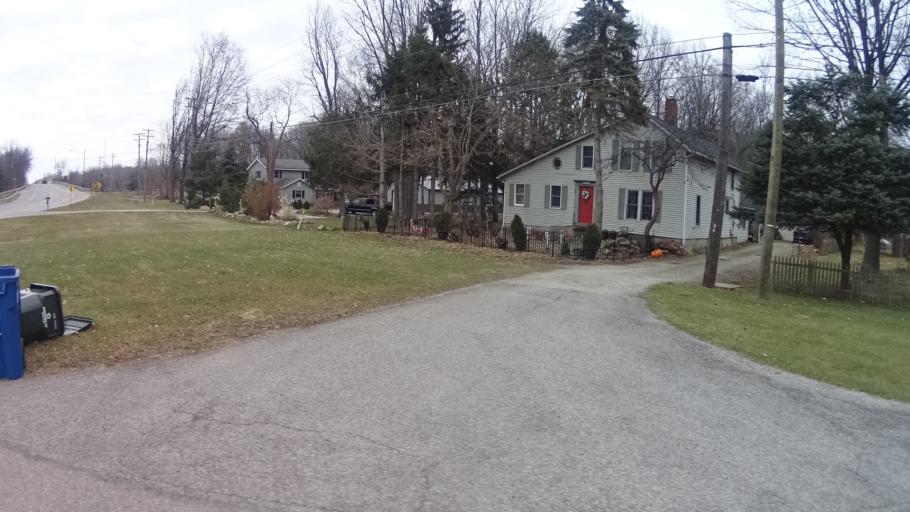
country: US
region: Ohio
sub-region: Lorain County
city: North Ridgeville
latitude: 41.3774
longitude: -82.0189
